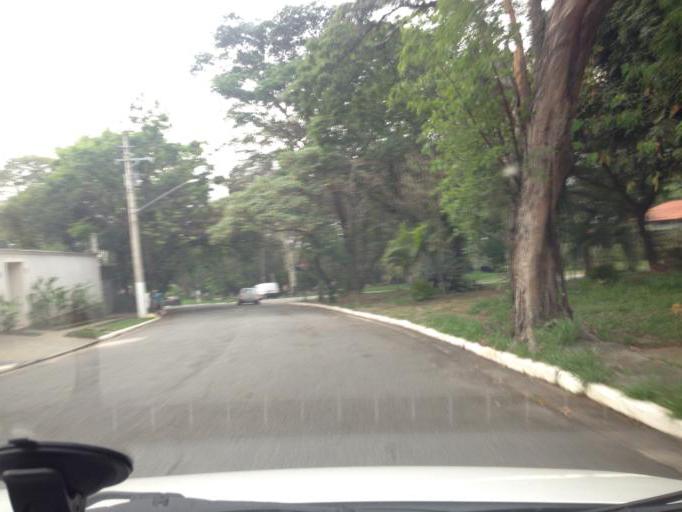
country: BR
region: Sao Paulo
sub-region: Osasco
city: Osasco
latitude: -23.5298
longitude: -46.7153
